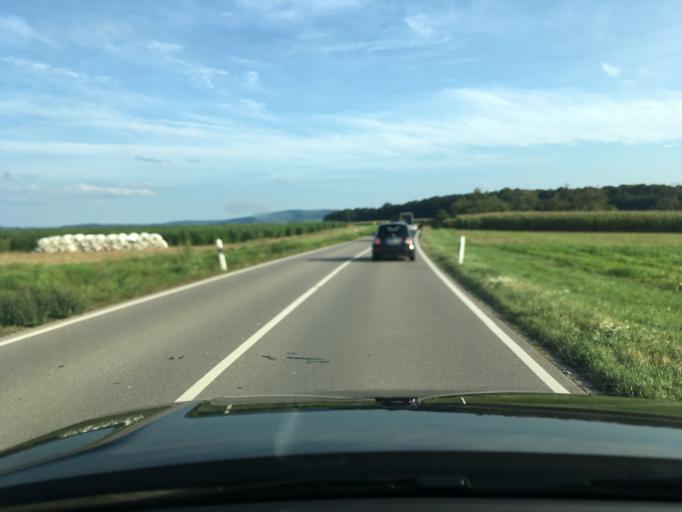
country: DE
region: Baden-Wuerttemberg
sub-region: Regierungsbezirk Stuttgart
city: Affalterbach
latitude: 48.9097
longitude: 9.3400
